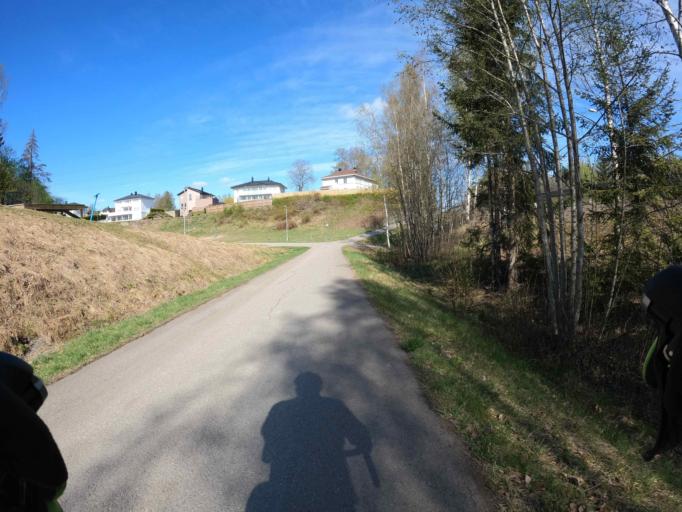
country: NO
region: Akershus
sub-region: Skedsmo
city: Lillestrom
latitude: 59.9735
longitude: 11.0042
